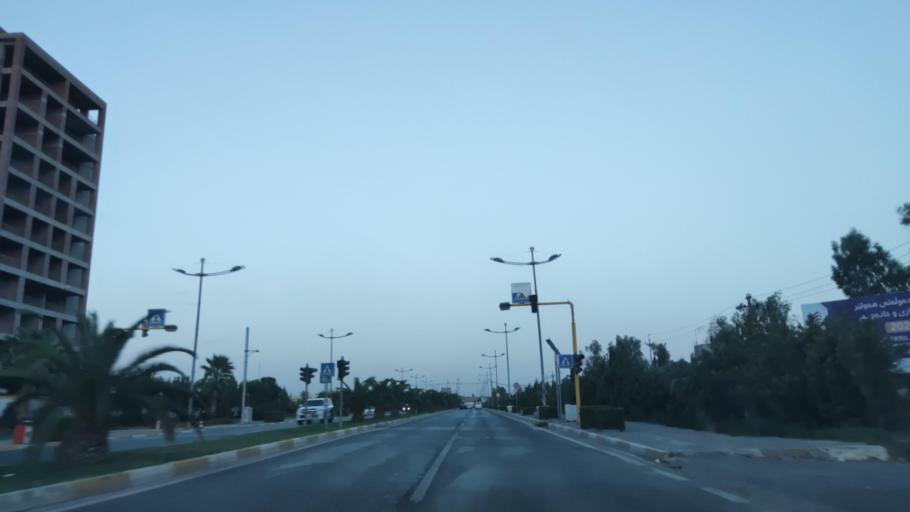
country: IQ
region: Arbil
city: Erbil
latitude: 36.1982
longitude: 43.9856
